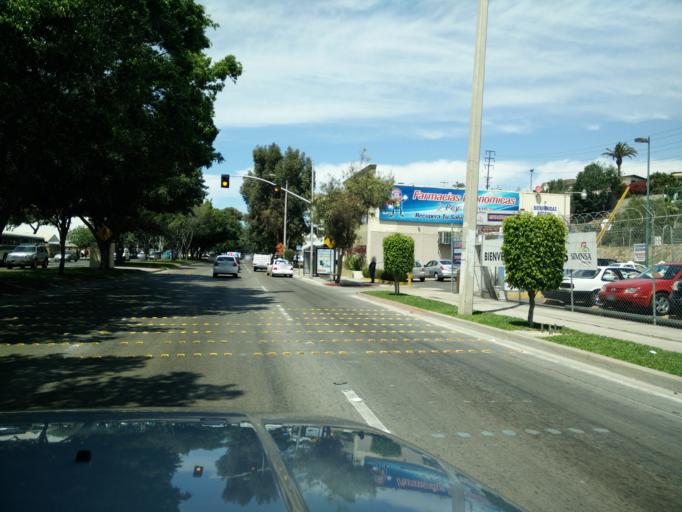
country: MX
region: Baja California
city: Tijuana
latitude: 32.5260
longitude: -117.0086
